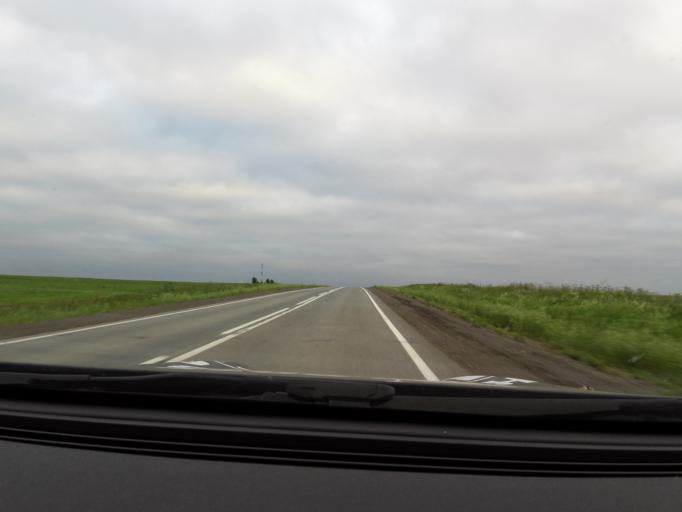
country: RU
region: Perm
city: Zyukayka
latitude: 58.3071
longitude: 54.7509
